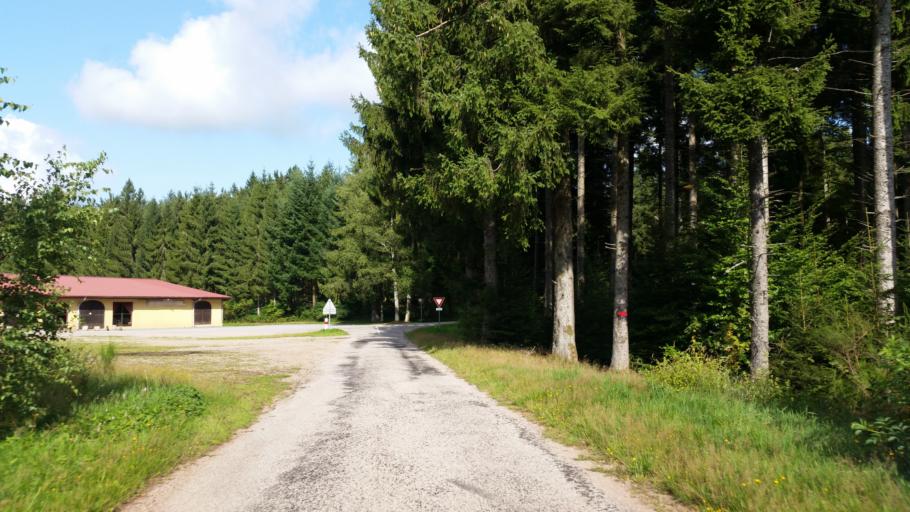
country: FR
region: Lorraine
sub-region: Departement des Vosges
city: Vecoux
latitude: 47.9747
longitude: 6.5982
